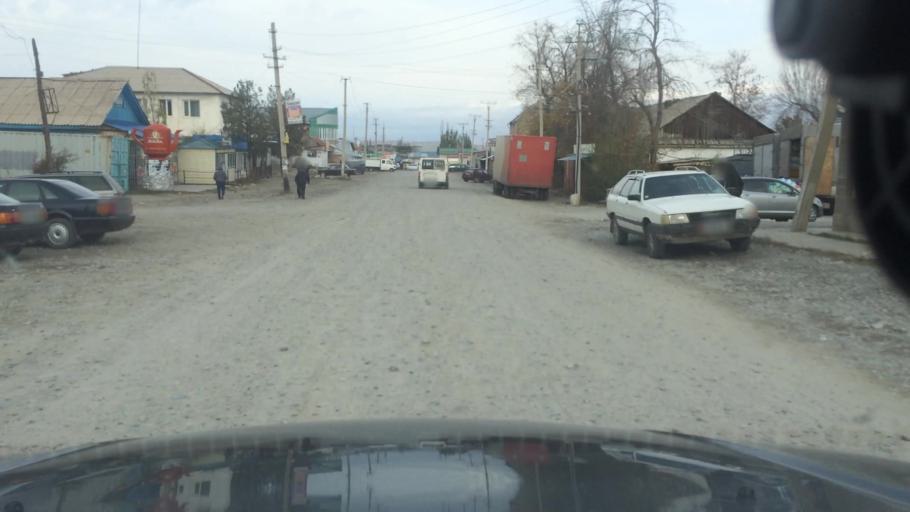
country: KG
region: Ysyk-Koel
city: Karakol
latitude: 42.4908
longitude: 78.3872
